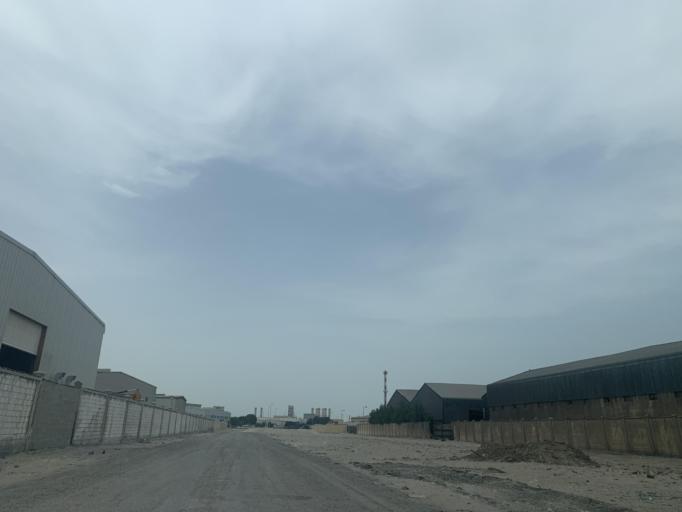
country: BH
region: Muharraq
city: Al Hadd
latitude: 26.2074
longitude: 50.6690
